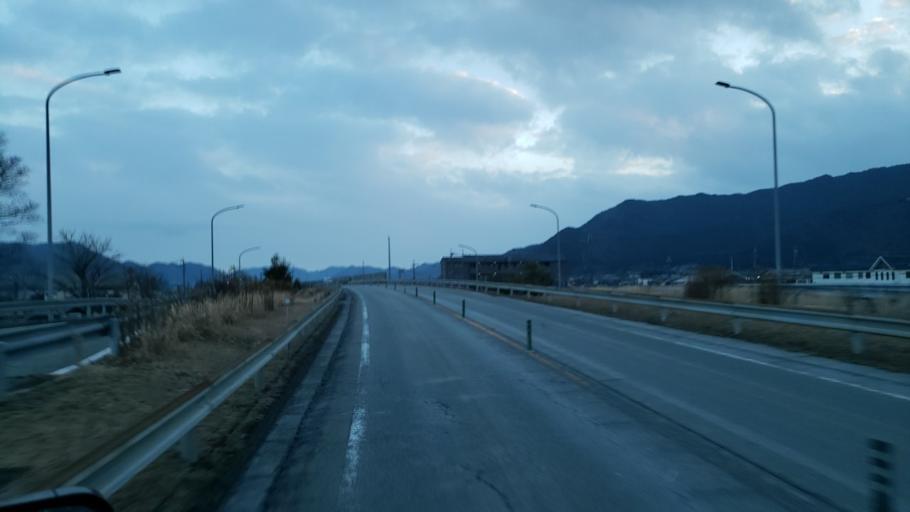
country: JP
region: Hyogo
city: Yamazakicho-nakabirose
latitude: 35.0588
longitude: 134.7640
